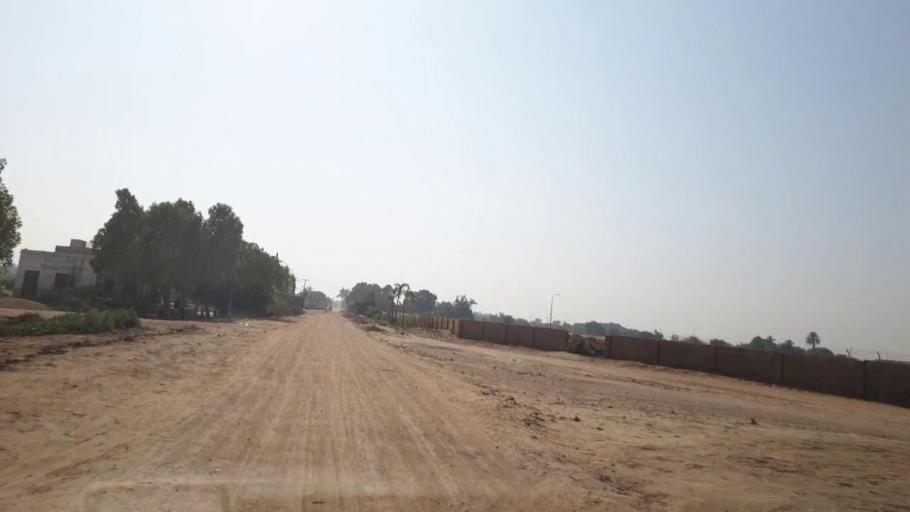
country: PK
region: Sindh
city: Thatta
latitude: 24.7597
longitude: 67.9163
